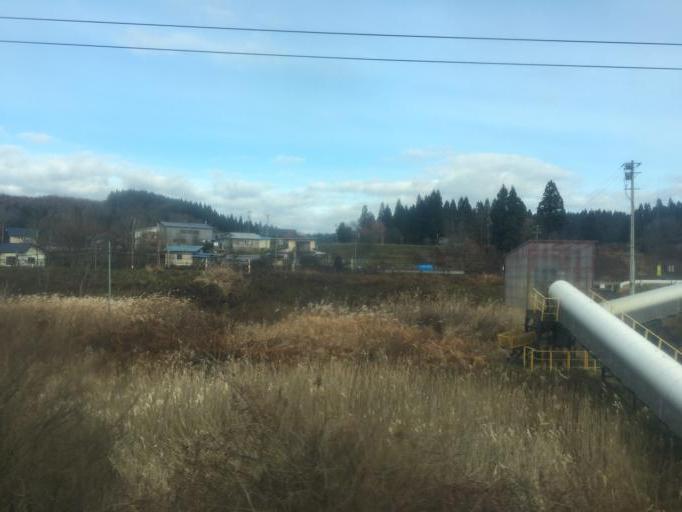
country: JP
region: Akita
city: Takanosu
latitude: 40.2639
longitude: 140.4219
